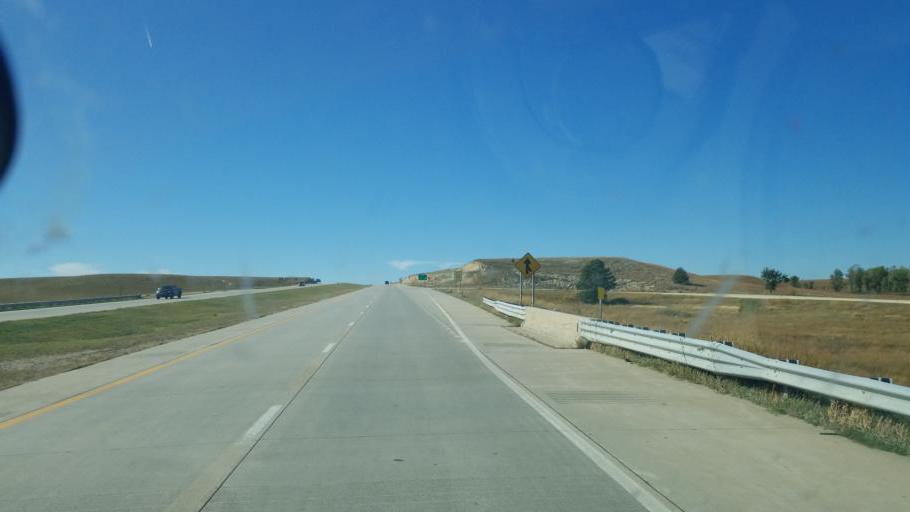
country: US
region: Kansas
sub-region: Riley County
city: Manhattan
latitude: 39.0657
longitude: -96.5760
